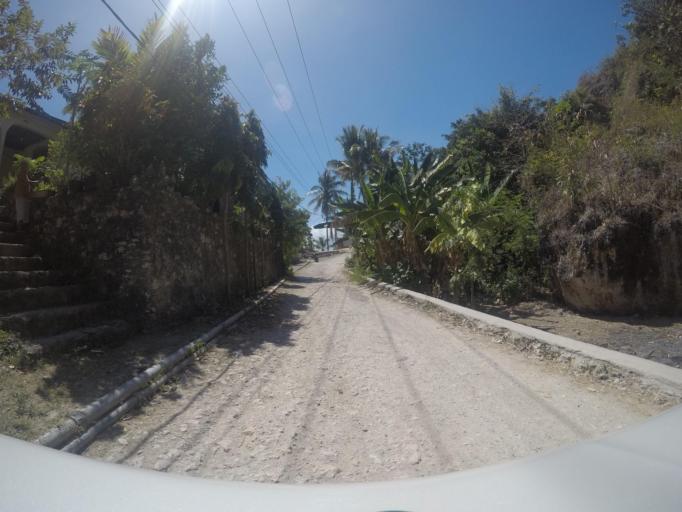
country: TL
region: Baucau
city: Baucau
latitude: -8.4646
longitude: 126.4553
